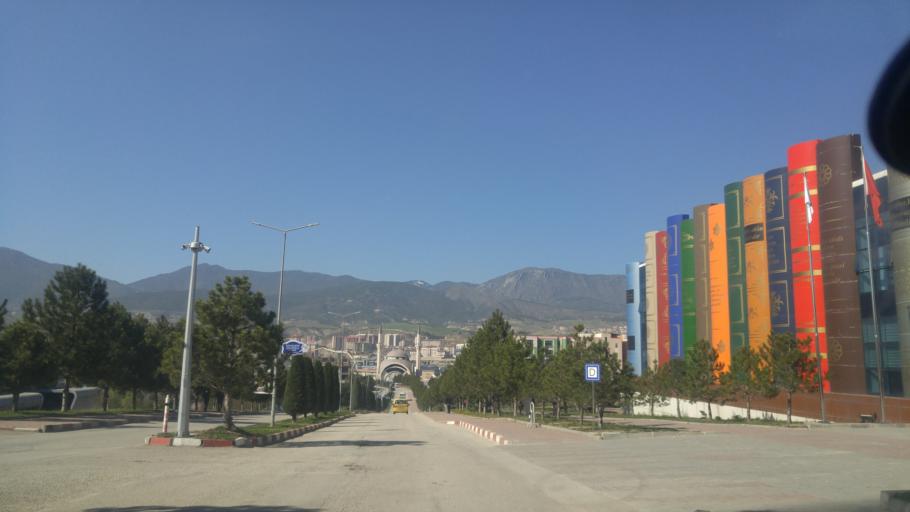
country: TR
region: Karabuk
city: Karabuk
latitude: 41.2077
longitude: 32.6574
